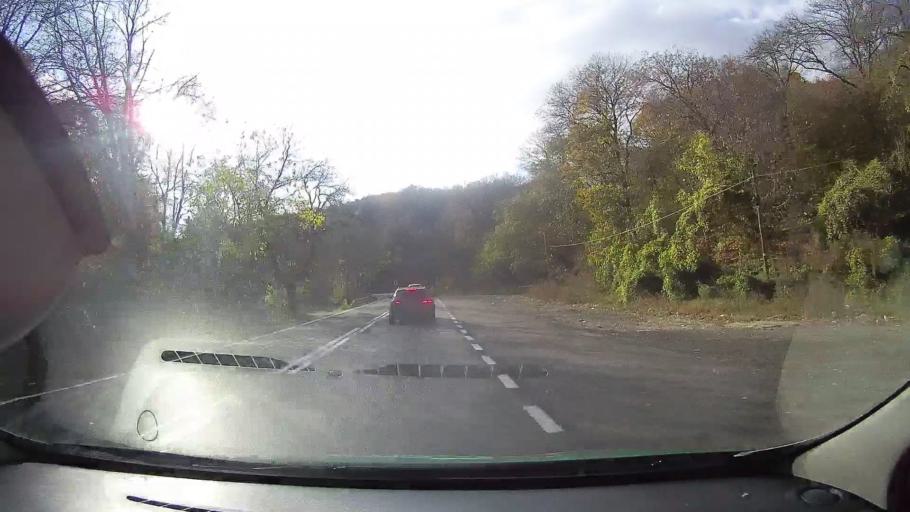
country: RO
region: Tulcea
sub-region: Comuna Ciucurova
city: Ciucurova
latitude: 44.9179
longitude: 28.4231
